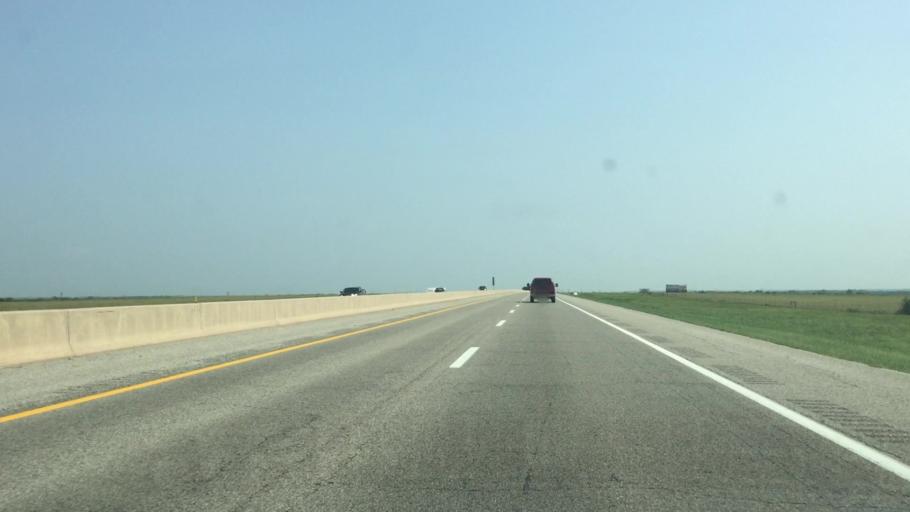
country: US
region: Kansas
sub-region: Lyon County
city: Emporia
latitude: 38.3484
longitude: -96.2901
